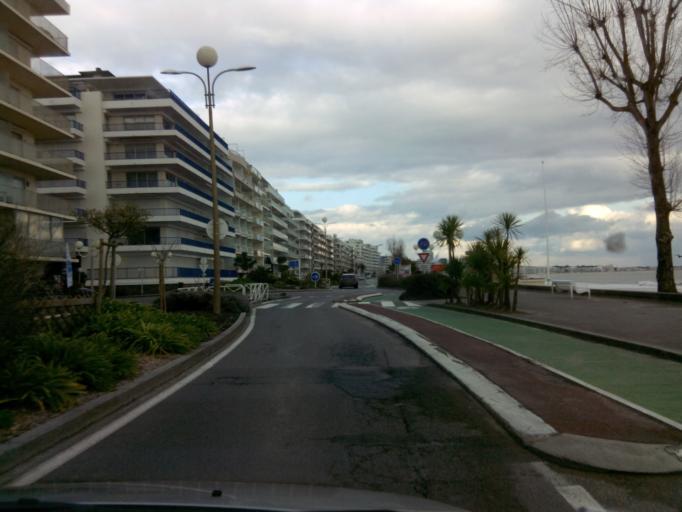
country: FR
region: Pays de la Loire
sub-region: Departement de la Loire-Atlantique
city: Le Pouliguen
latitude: 47.2815
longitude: -2.4006
